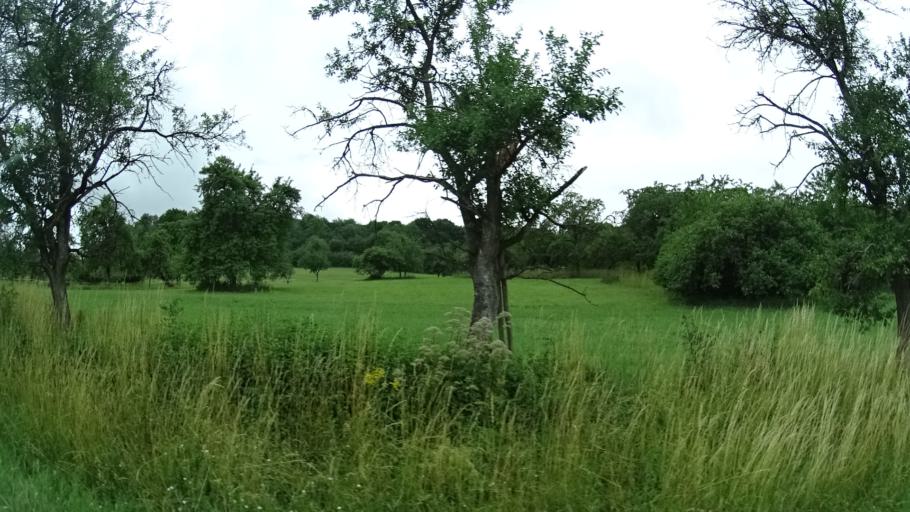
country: DE
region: Saarland
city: Orscholz
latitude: 49.4644
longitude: 6.5064
